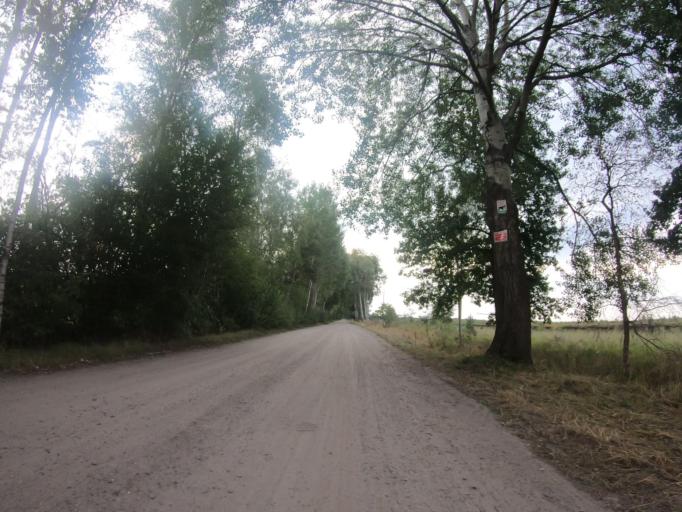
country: DE
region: Lower Saxony
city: Sassenburg
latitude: 52.5645
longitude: 10.6293
